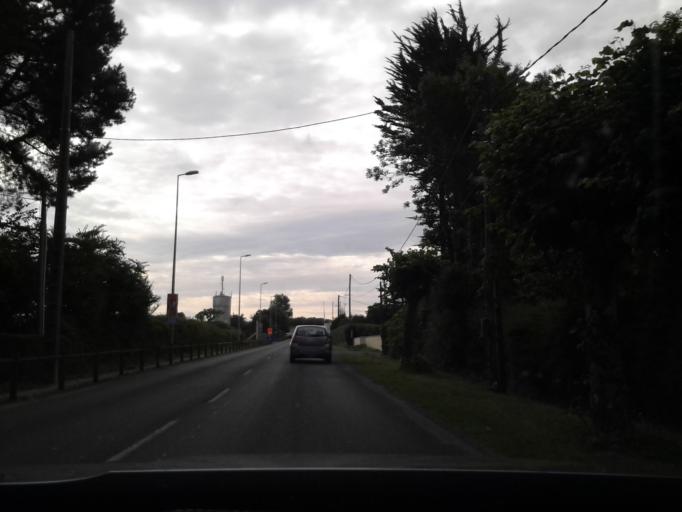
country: FR
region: Lower Normandy
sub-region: Departement de la Manche
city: Valognes
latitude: 49.5024
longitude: -1.4587
